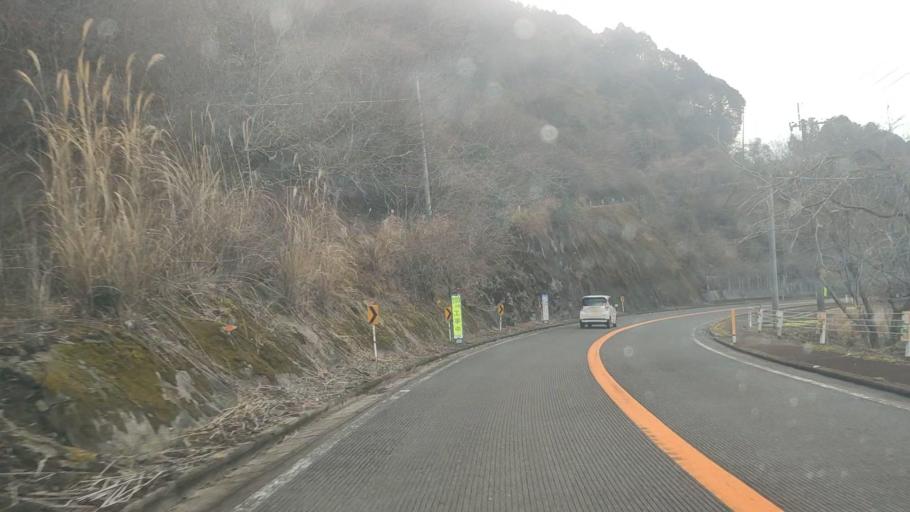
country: JP
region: Kumamoto
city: Hitoyoshi
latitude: 32.0826
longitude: 130.8009
